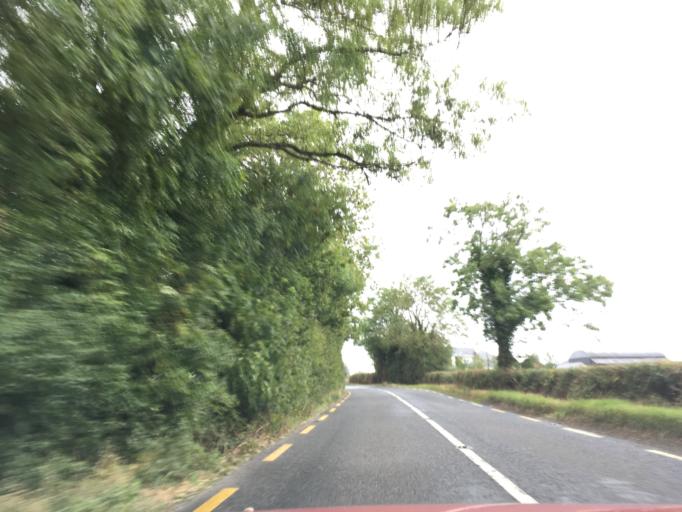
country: IE
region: Munster
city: Fethard
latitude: 52.4280
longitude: -7.7773
